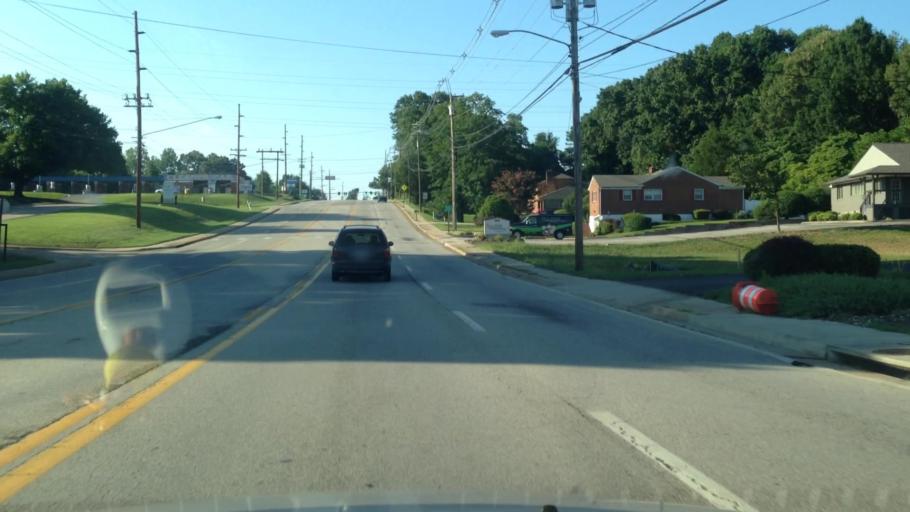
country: US
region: Virginia
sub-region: City of Danville
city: Danville
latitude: 36.6143
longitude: -79.4056
